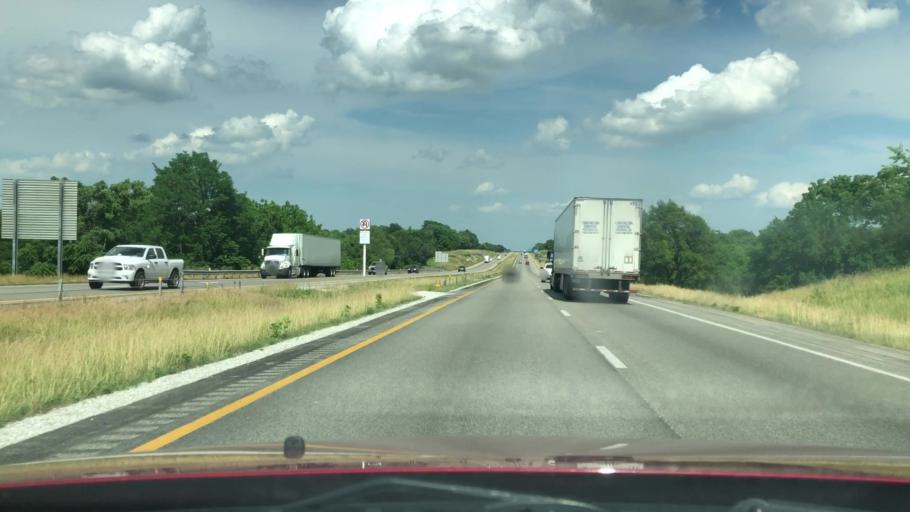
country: US
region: Missouri
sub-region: Greene County
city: Springfield
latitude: 37.2502
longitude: -93.2934
